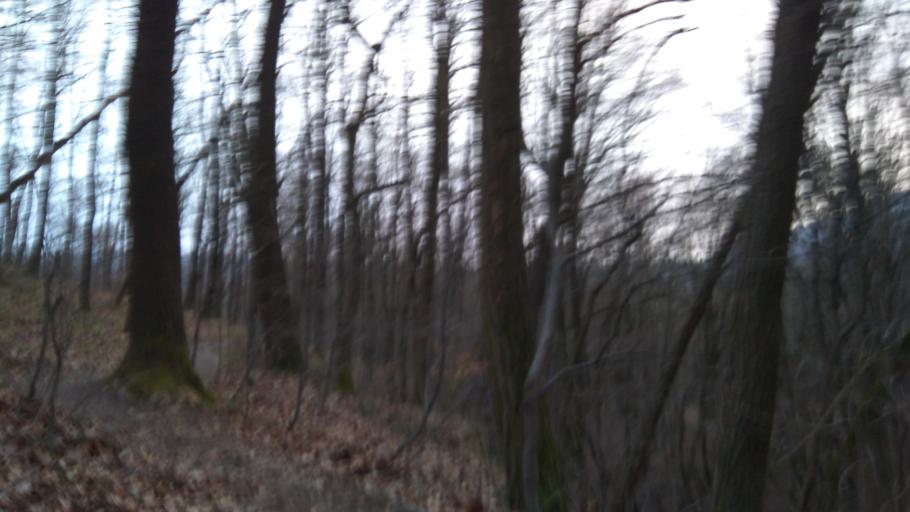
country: HU
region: Pest
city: Pilisszentkereszt
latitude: 47.6919
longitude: 18.9138
